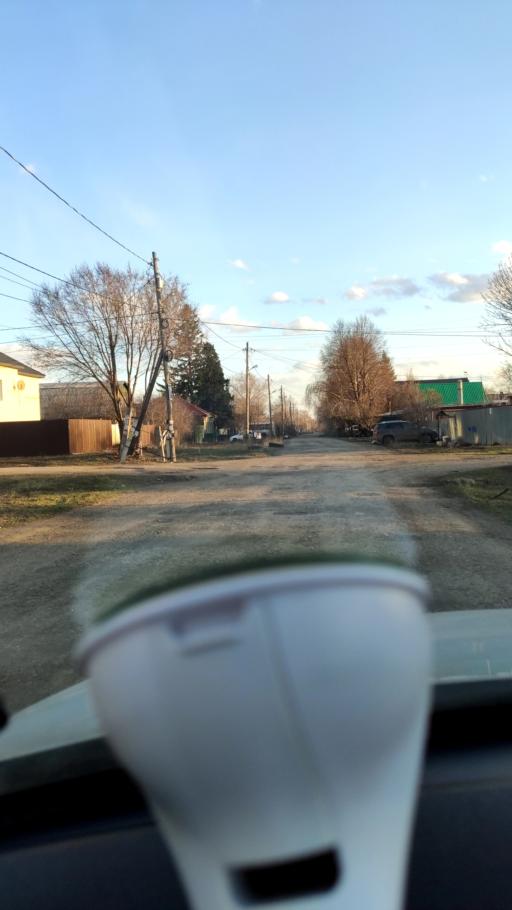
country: RU
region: Samara
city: Smyshlyayevka
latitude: 53.2508
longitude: 50.3432
